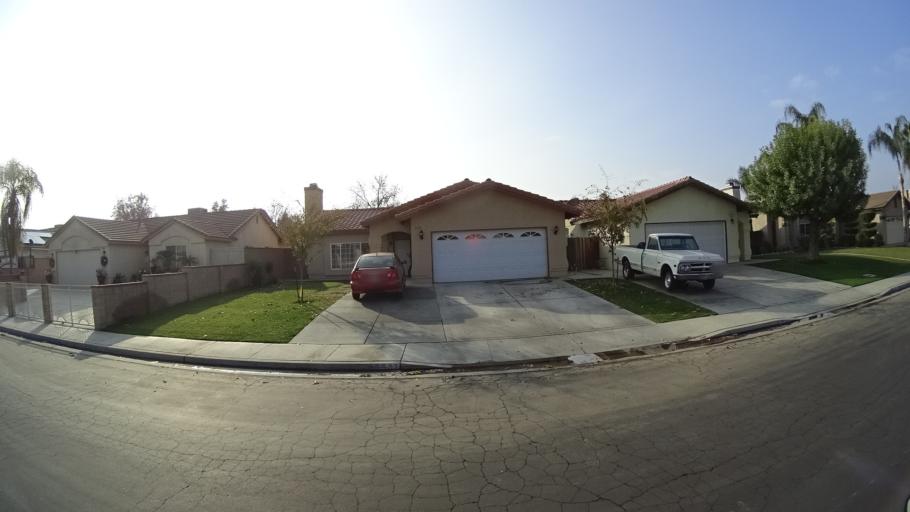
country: US
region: California
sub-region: Kern County
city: Greenfield
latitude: 35.3038
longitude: -119.0640
